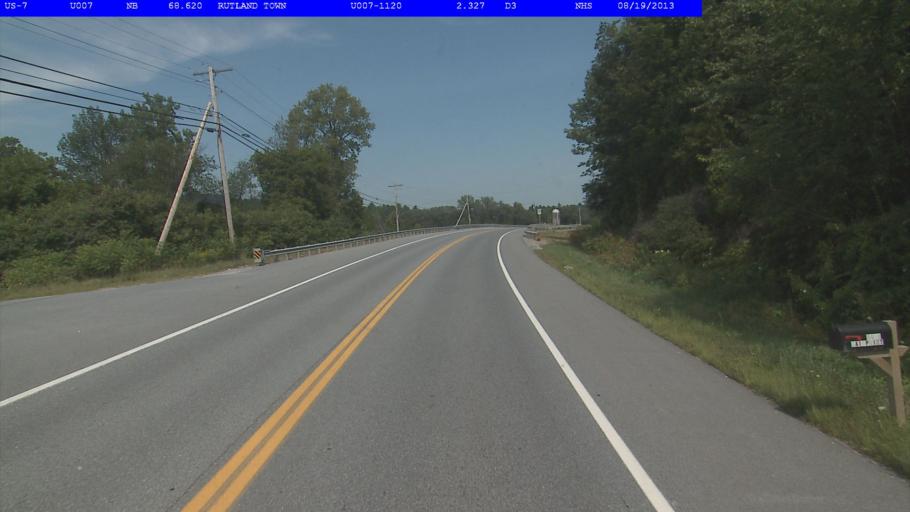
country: US
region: Vermont
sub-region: Rutland County
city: Rutland
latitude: 43.6445
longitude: -72.9844
